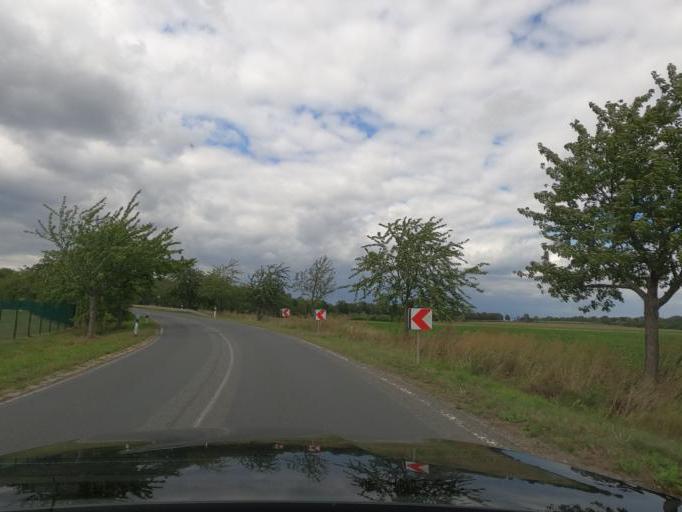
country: DE
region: Lower Saxony
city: Algermissen
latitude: 52.2655
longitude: 9.9606
